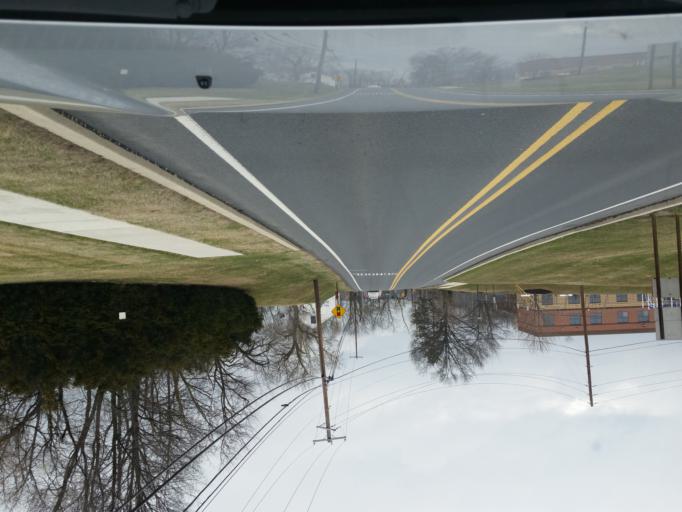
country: US
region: Pennsylvania
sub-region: Dauphin County
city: Paxtonia
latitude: 40.3194
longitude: -76.7803
